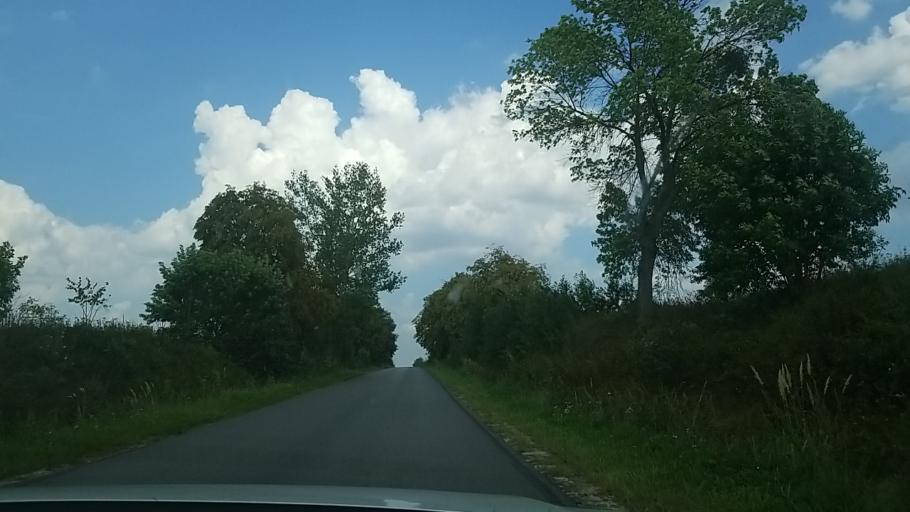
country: PL
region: Lublin Voivodeship
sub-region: Powiat janowski
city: Dzwola
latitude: 50.7101
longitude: 22.5816
